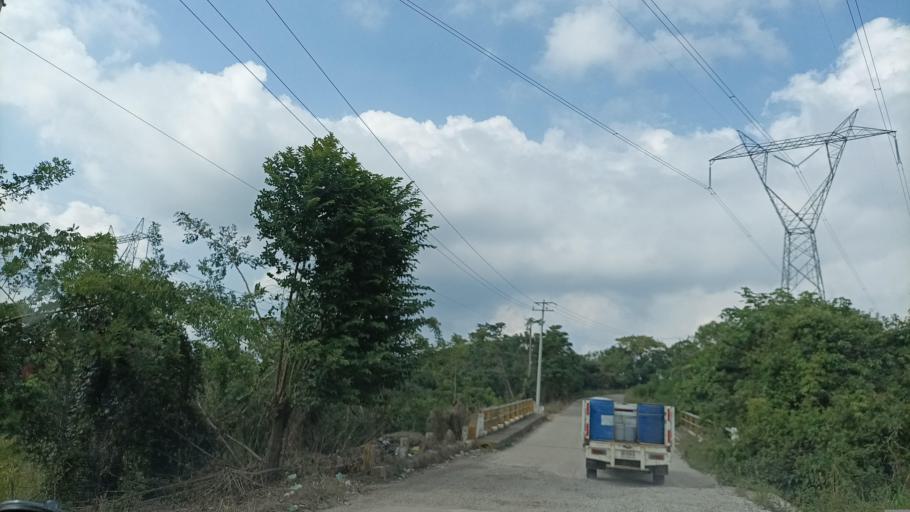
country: MX
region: Veracruz
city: Las Choapas
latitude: 17.7986
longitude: -94.1101
